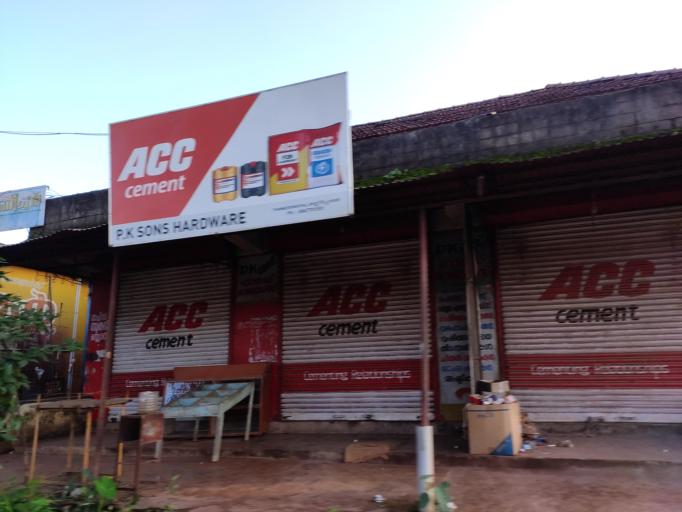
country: IN
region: Kerala
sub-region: Palakkad district
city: Mannarakkat
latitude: 10.9317
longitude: 76.4734
